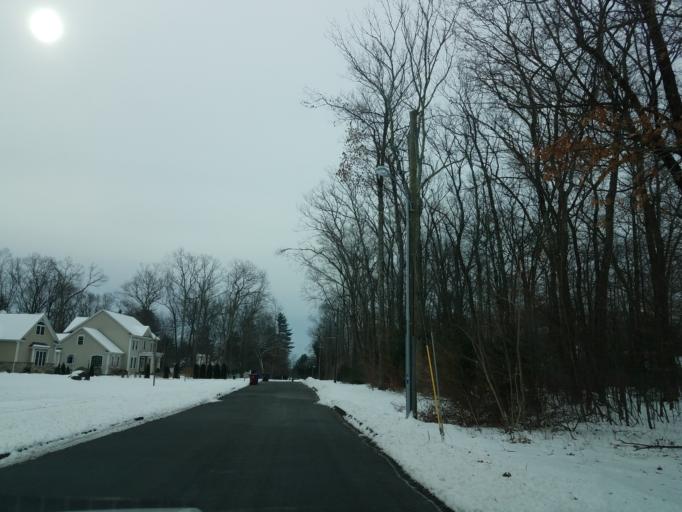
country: US
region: Connecticut
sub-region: Hartford County
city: Farmington
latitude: 41.7224
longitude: -72.8768
